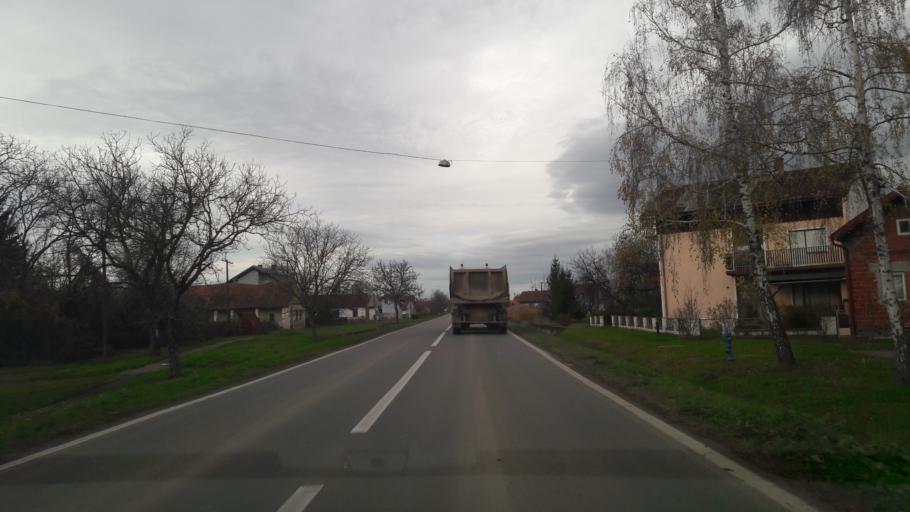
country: HR
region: Osjecko-Baranjska
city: Fericanci
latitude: 45.5252
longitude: 17.9649
